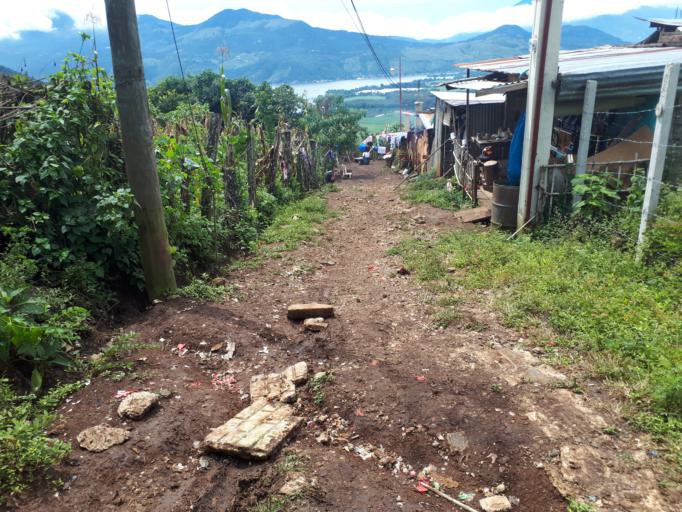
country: GT
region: Guatemala
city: Villa Canales
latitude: 14.4580
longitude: -90.5124
